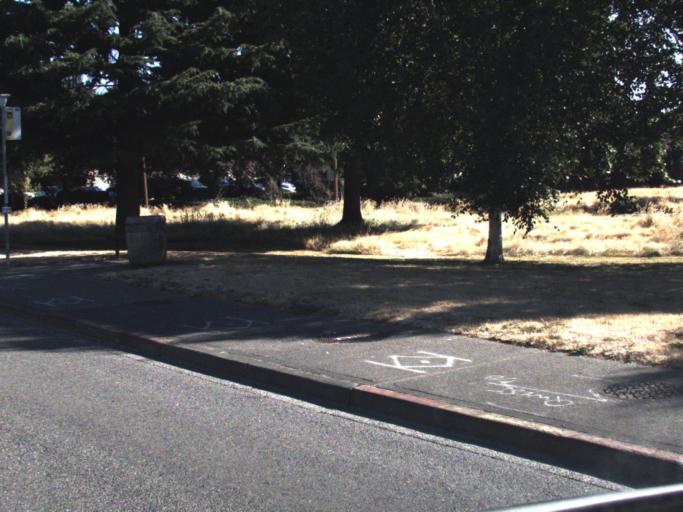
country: US
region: Washington
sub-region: King County
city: SeaTac
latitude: 47.4273
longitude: -122.2494
